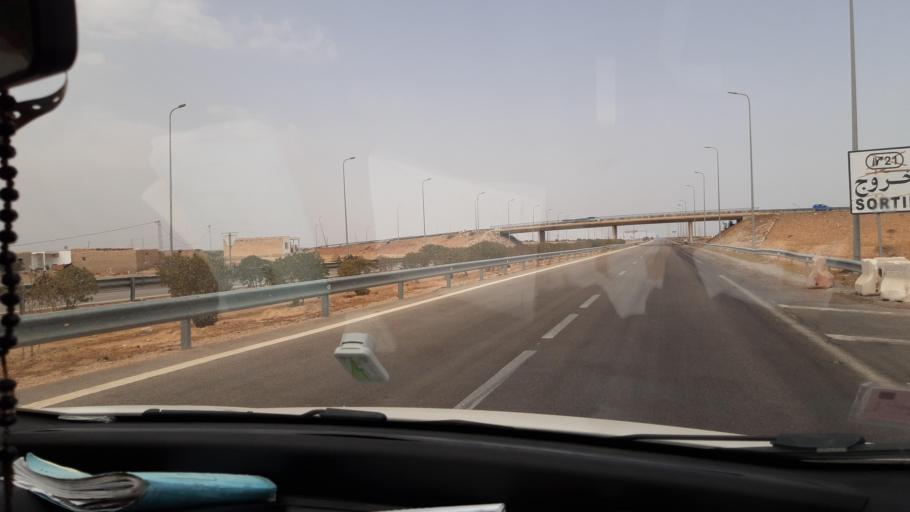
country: TN
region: Safaqis
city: Al Qarmadah
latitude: 34.8905
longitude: 10.7151
